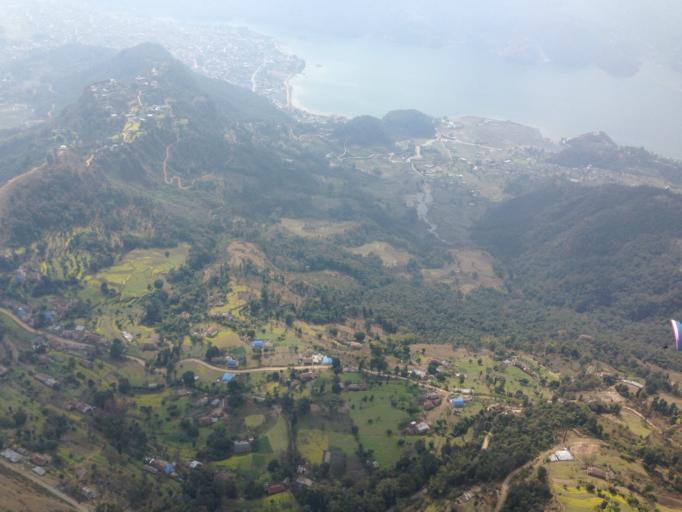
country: NP
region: Western Region
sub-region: Gandaki Zone
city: Pokhara
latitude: 28.2420
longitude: 83.9647
